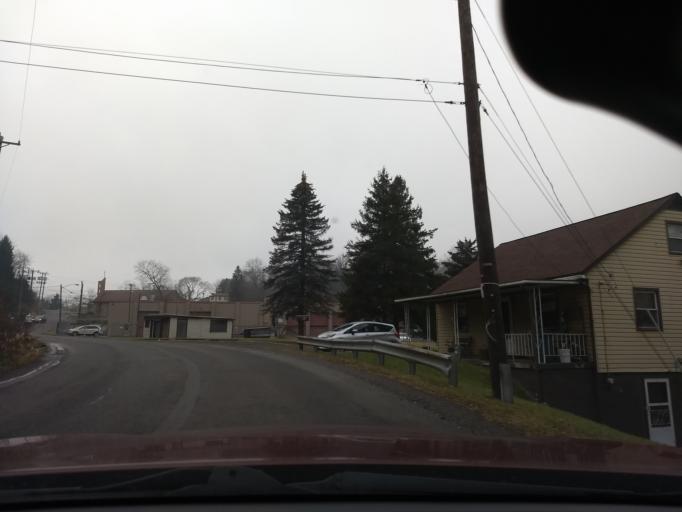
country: US
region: Pennsylvania
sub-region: Allegheny County
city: East Pittsburgh
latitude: 40.3860
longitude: -79.8308
